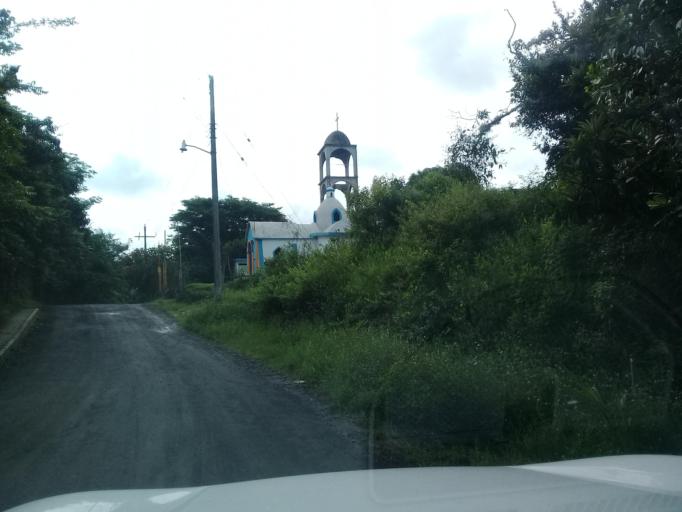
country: MX
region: Veracruz
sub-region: Emiliano Zapata
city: Jacarandas
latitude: 19.4810
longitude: -96.8548
